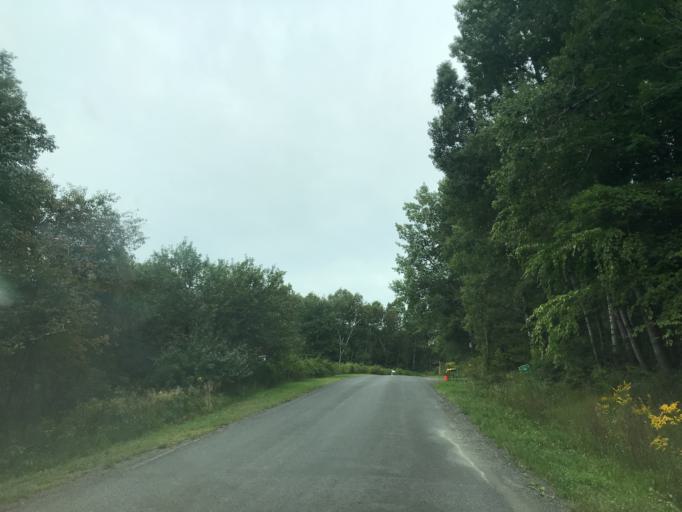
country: US
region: New York
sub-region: Otsego County
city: Worcester
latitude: 42.5899
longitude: -74.6801
